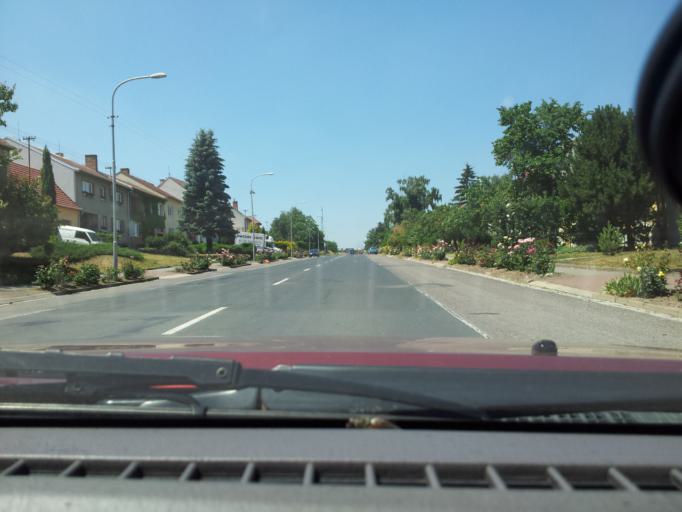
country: CZ
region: South Moravian
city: Klobouky
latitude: 48.9969
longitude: 16.8816
